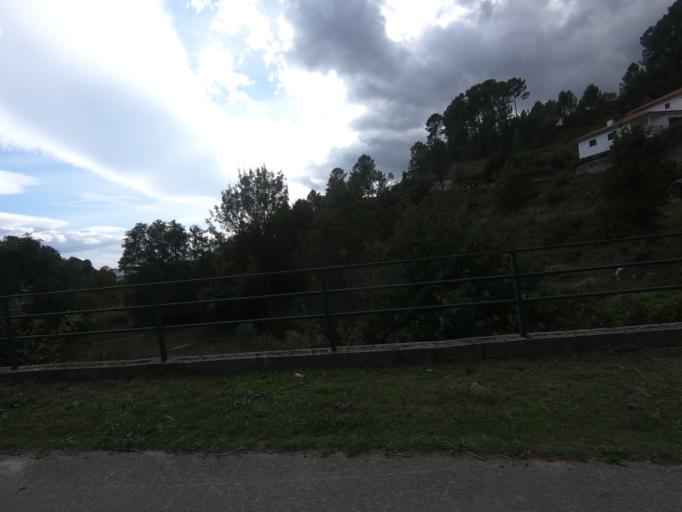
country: PT
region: Vila Real
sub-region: Vila Real
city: Vila Real
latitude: 41.3227
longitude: -7.7707
